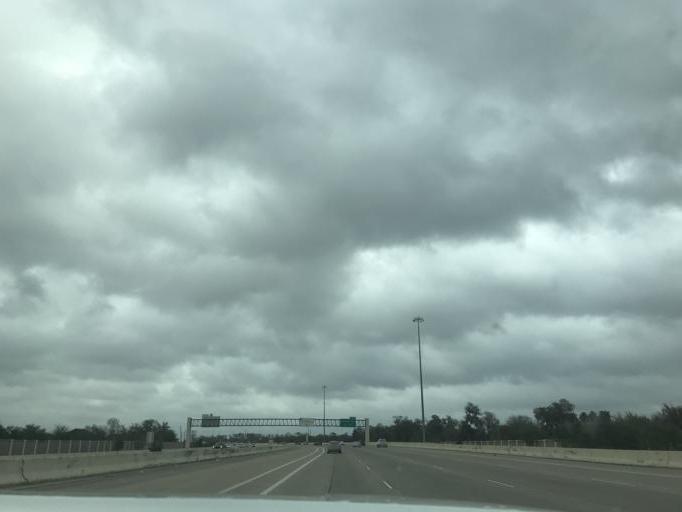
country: US
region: Texas
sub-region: Fort Bend County
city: Greatwood
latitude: 29.5638
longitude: -95.6776
